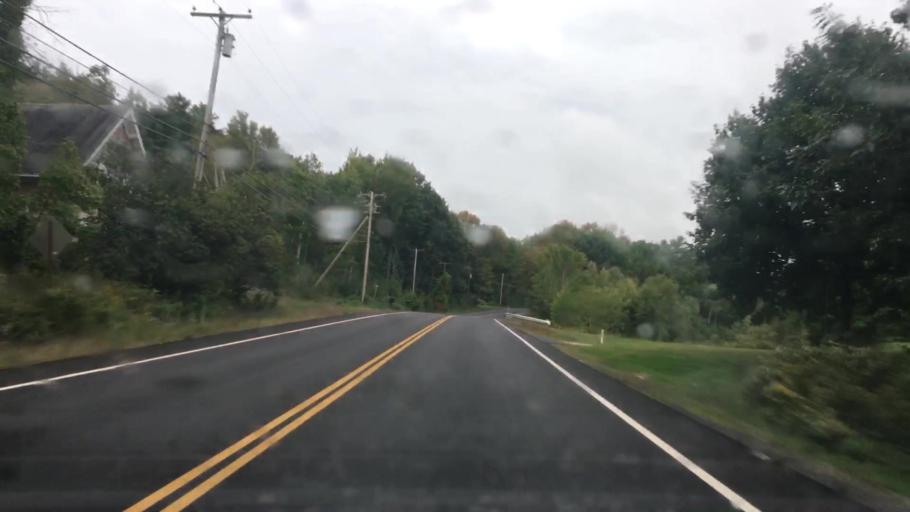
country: US
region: Maine
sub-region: Penobscot County
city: Orrington
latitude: 44.6824
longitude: -68.8094
